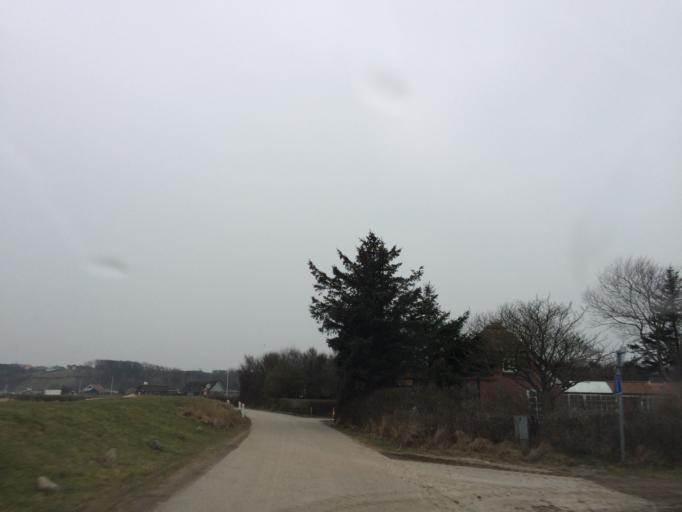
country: DK
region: Central Jutland
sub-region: Lemvig Kommune
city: Lemvig
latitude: 56.5872
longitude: 8.2857
